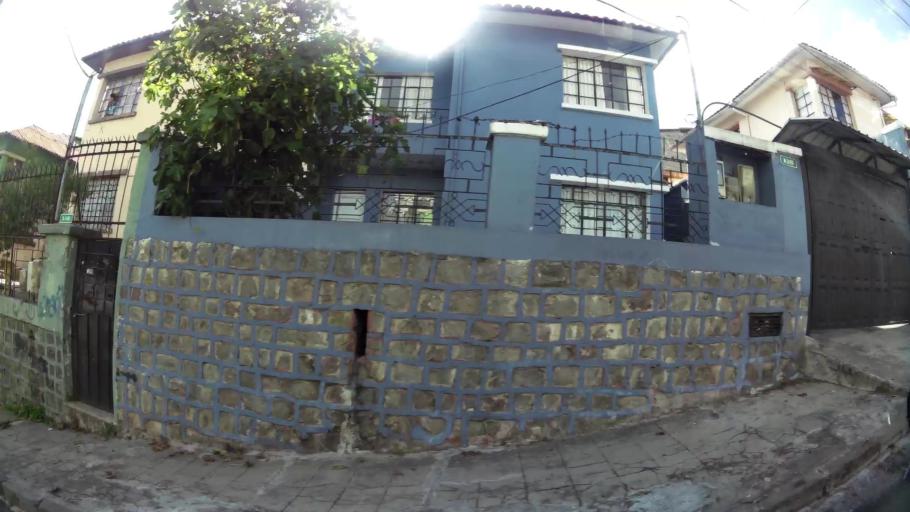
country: EC
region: Pichincha
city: Quito
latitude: -0.2264
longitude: -78.5023
